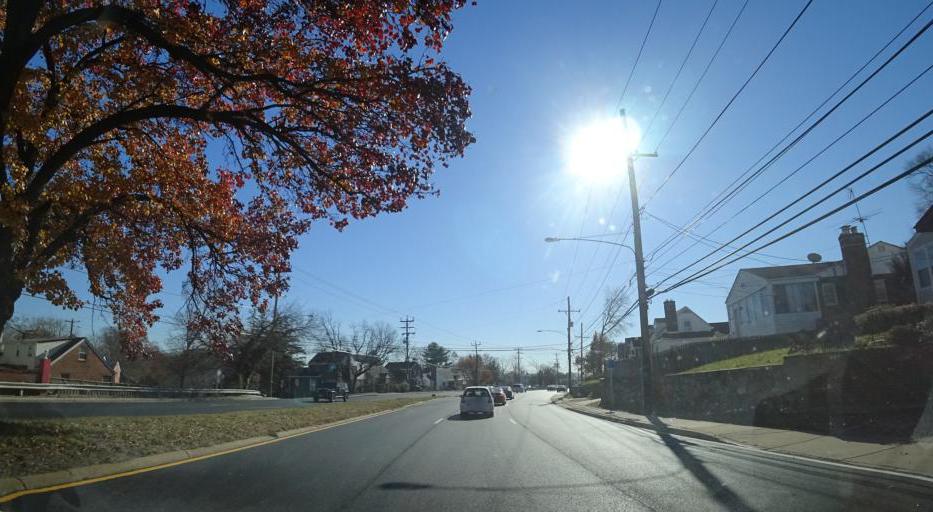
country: US
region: Maryland
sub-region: Prince George's County
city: Langley Park
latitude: 39.0031
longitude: -76.9962
